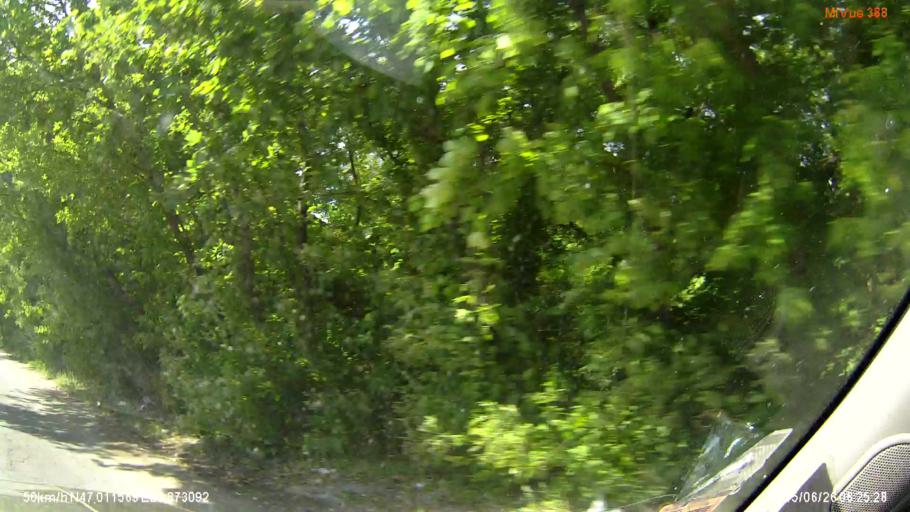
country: MD
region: Chisinau
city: Chisinau
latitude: 47.0117
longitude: 28.8730
